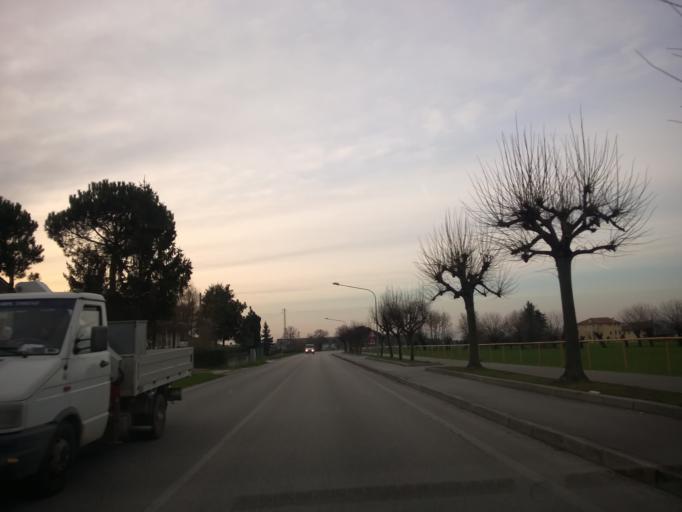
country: IT
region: Veneto
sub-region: Provincia di Vicenza
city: Carre
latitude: 45.7393
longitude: 11.4636
